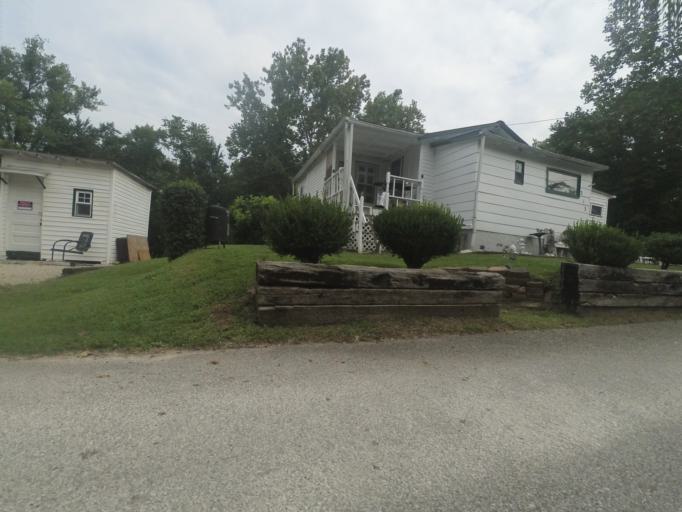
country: US
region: West Virginia
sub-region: Cabell County
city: Huntington
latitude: 38.4294
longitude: -82.4552
